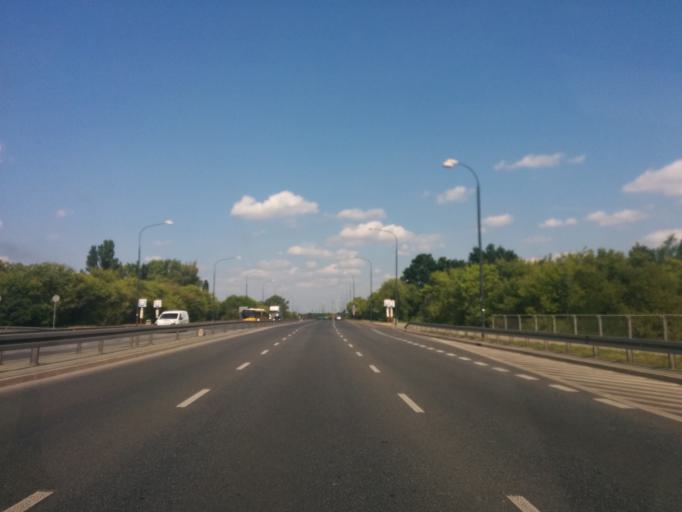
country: PL
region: Masovian Voivodeship
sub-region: Warszawa
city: Zoliborz
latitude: 52.2989
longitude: 20.9942
